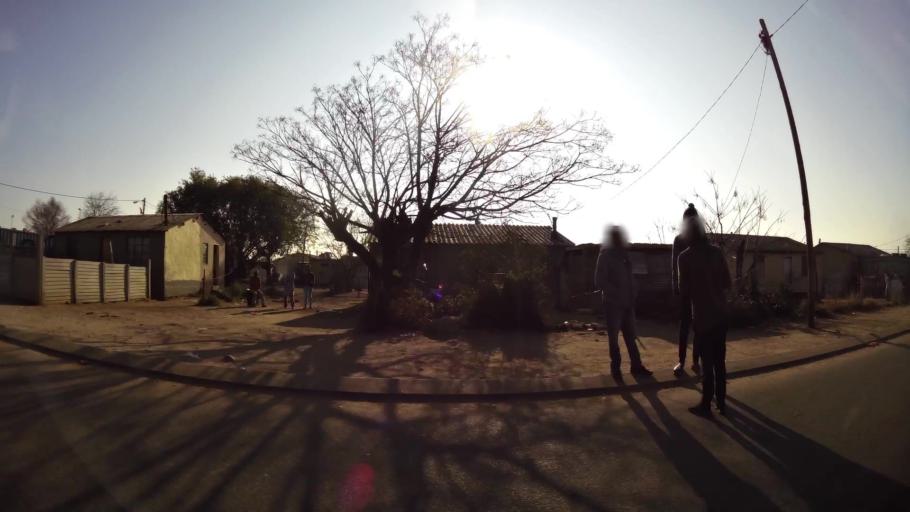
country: ZA
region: Orange Free State
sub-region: Mangaung Metropolitan Municipality
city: Bloemfontein
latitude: -29.1395
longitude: 26.2482
